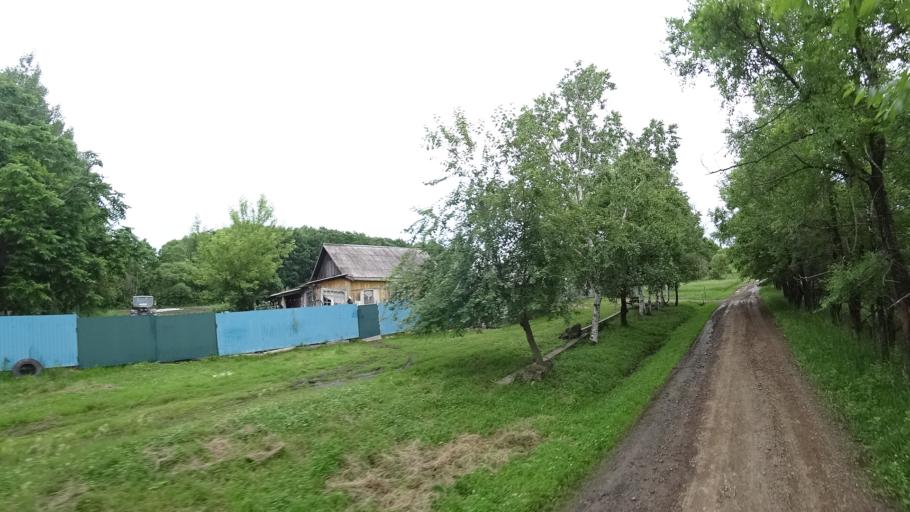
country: RU
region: Primorskiy
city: Novosysoyevka
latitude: 44.2444
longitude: 133.3800
